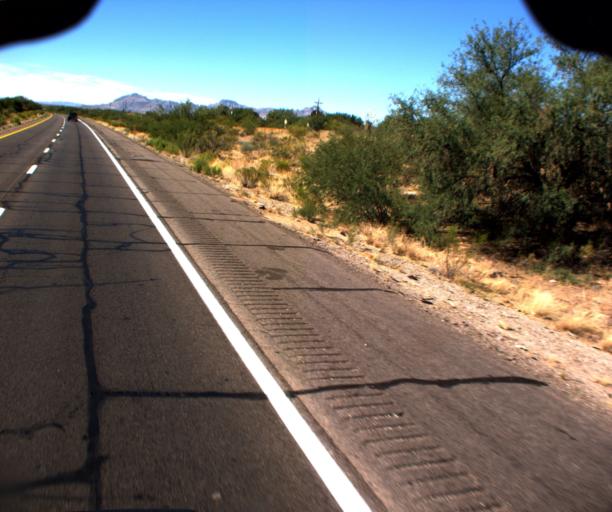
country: US
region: Arizona
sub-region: Pima County
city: Arivaca Junction
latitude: 31.7042
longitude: -111.0656
